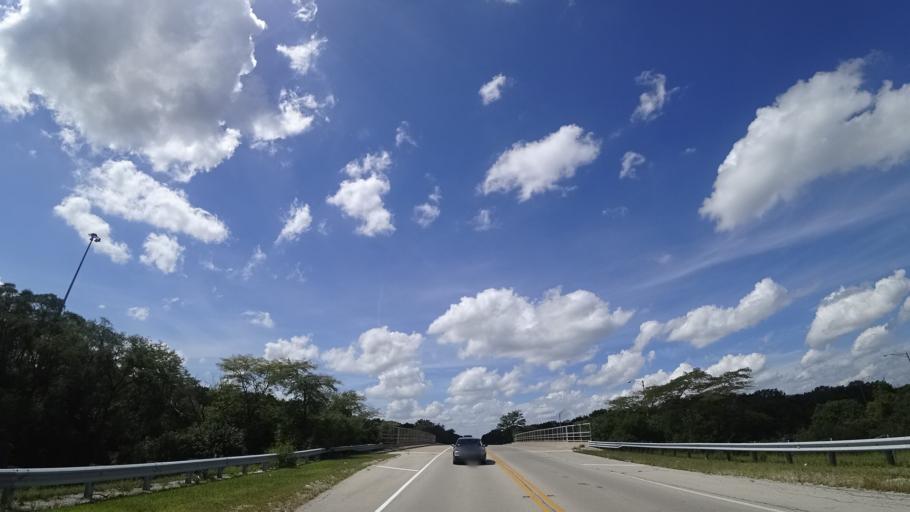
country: US
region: Illinois
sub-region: Cook County
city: Country Club Hills
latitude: 41.5570
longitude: -87.7424
